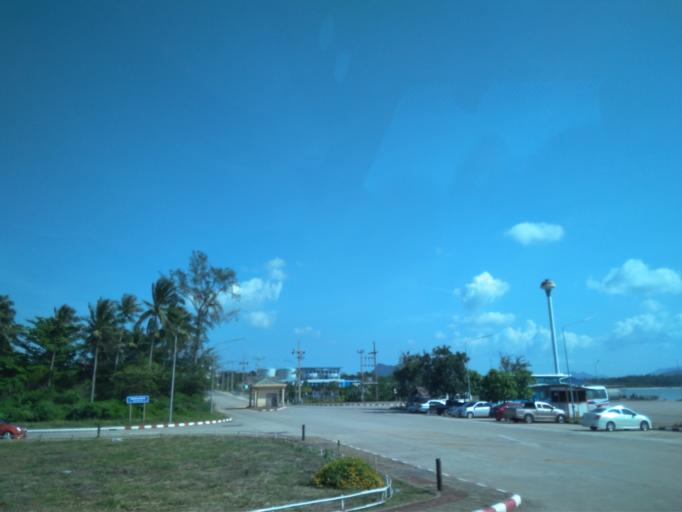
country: TH
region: Surat Thani
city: Don Sak
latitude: 9.3372
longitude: 99.6813
